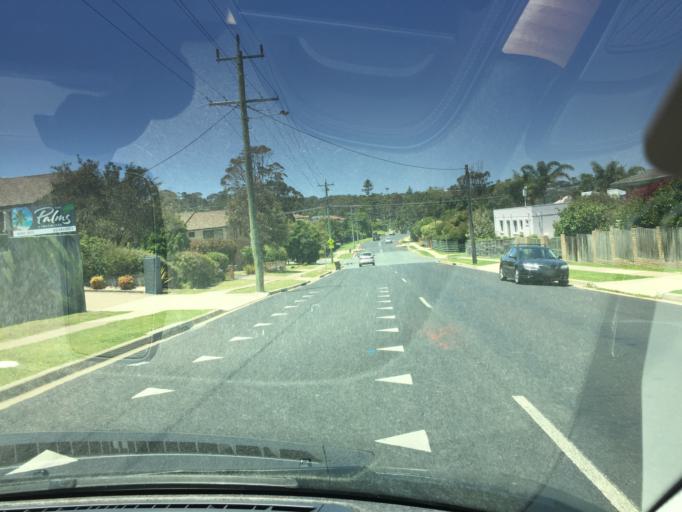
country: AU
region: New South Wales
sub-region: Bega Valley
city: Merimbula
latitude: -36.8868
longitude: 149.9147
